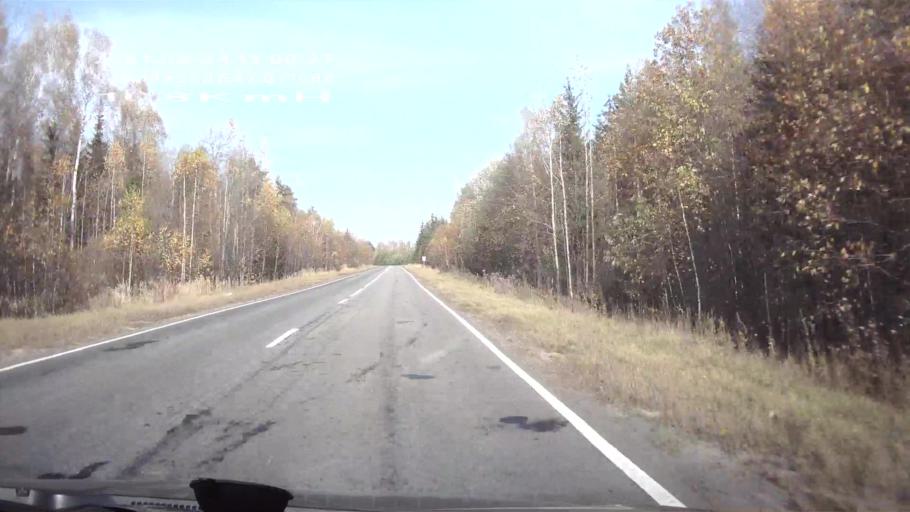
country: RU
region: Chuvashia
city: Buinsk
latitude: 55.1886
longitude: 47.0717
